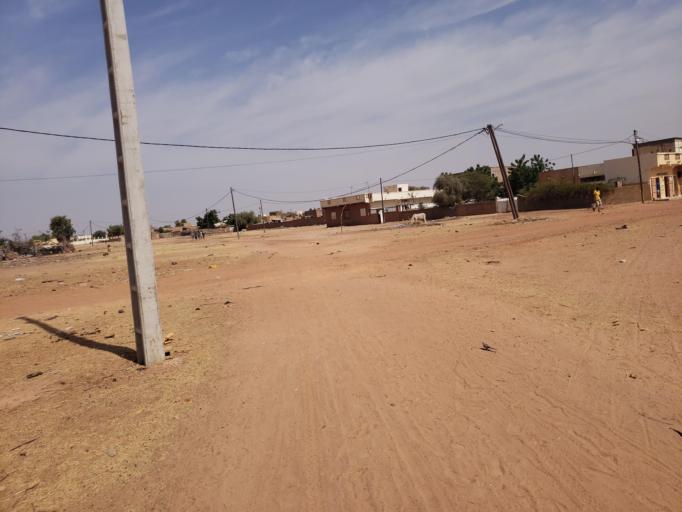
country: SN
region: Matam
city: Ranerou
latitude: 15.2998
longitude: -13.9601
